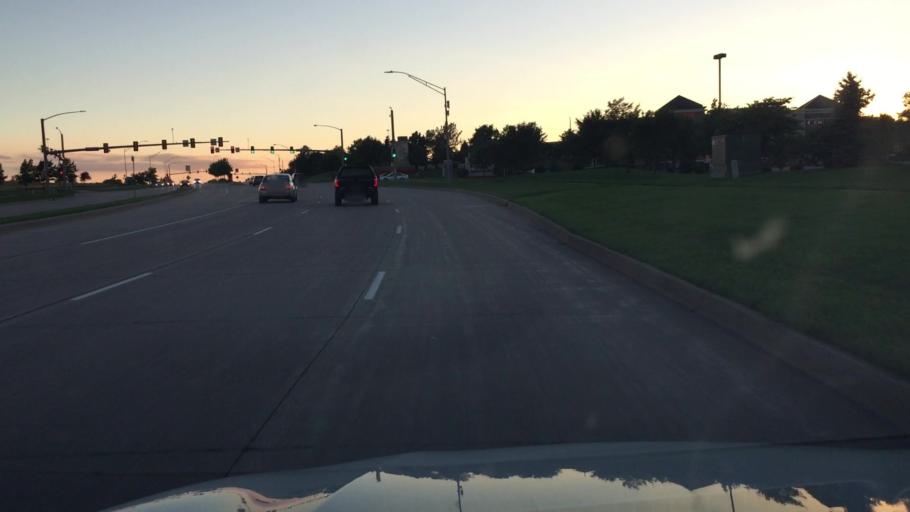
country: US
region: Iowa
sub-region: Polk County
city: Clive
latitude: 41.5620
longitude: -93.7982
